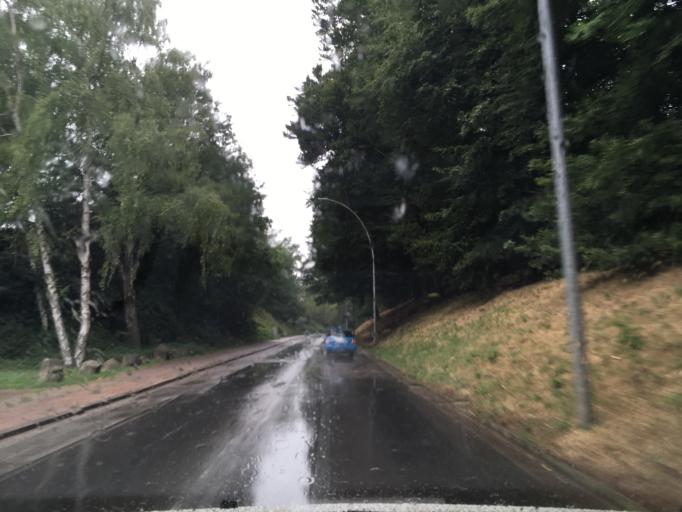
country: DE
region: Saarland
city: Sankt Ingbert
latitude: 49.2887
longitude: 7.1236
